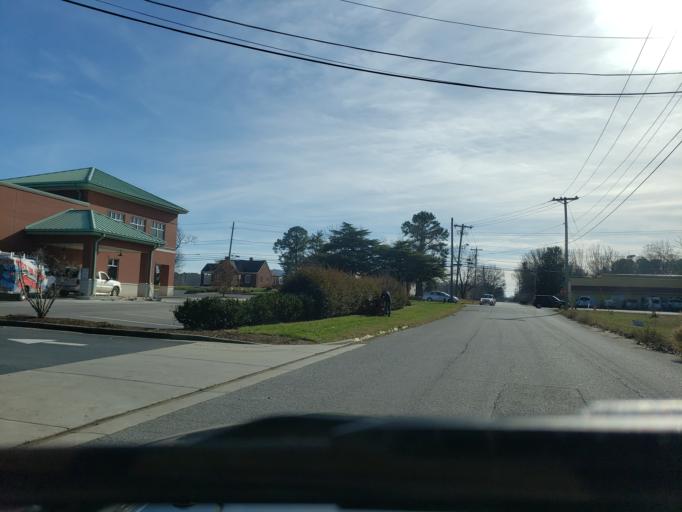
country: US
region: North Carolina
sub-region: Cleveland County
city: Kings Mountain
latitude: 35.2415
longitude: -81.3303
